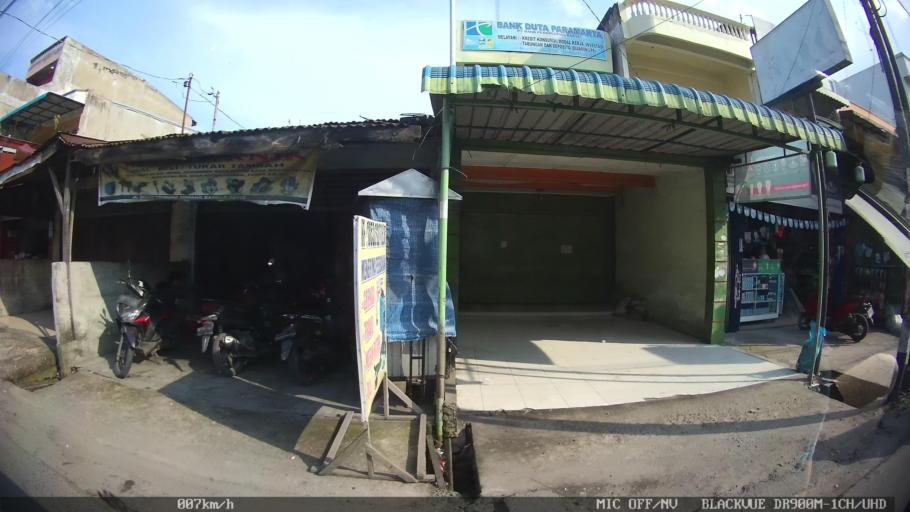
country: ID
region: North Sumatra
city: Medan
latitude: 3.5964
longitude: 98.7466
